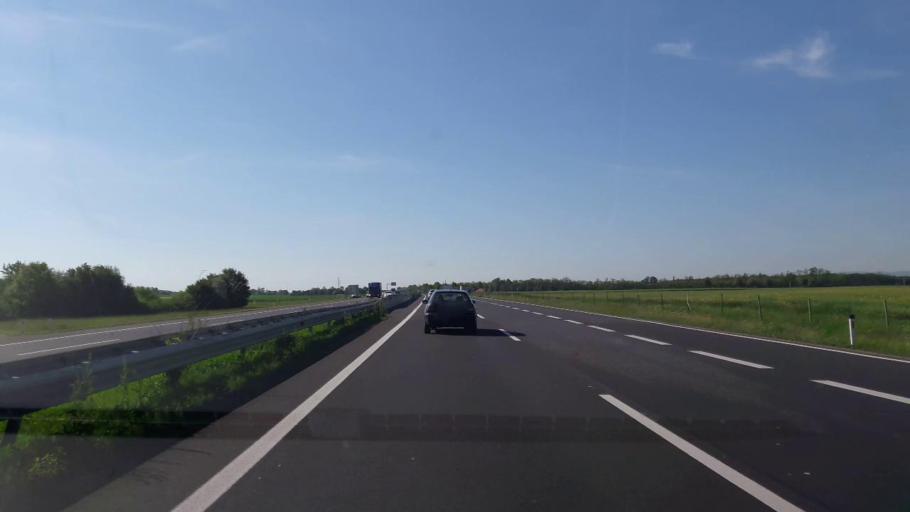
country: AT
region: Burgenland
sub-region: Eisenstadt-Umgebung
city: Hornstein
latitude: 47.8661
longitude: 16.4197
